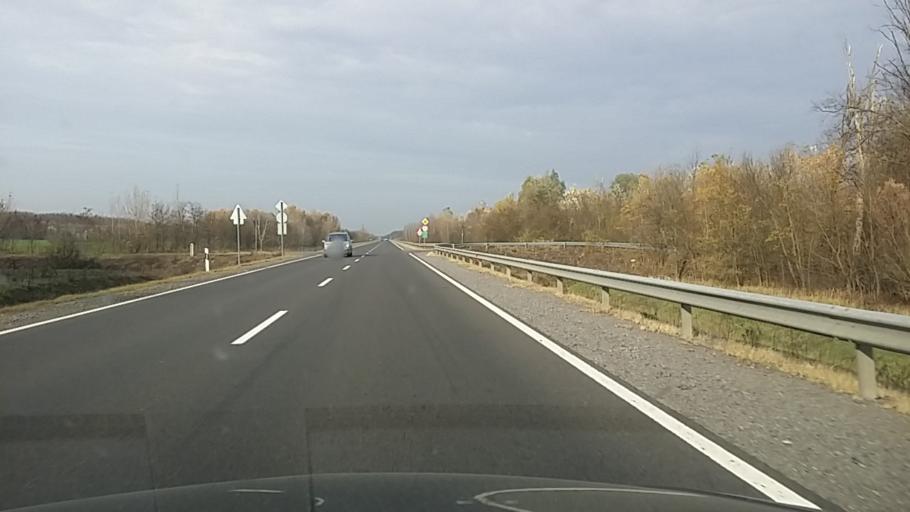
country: HU
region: Szabolcs-Szatmar-Bereg
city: Nagykallo
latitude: 47.9074
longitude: 21.8180
